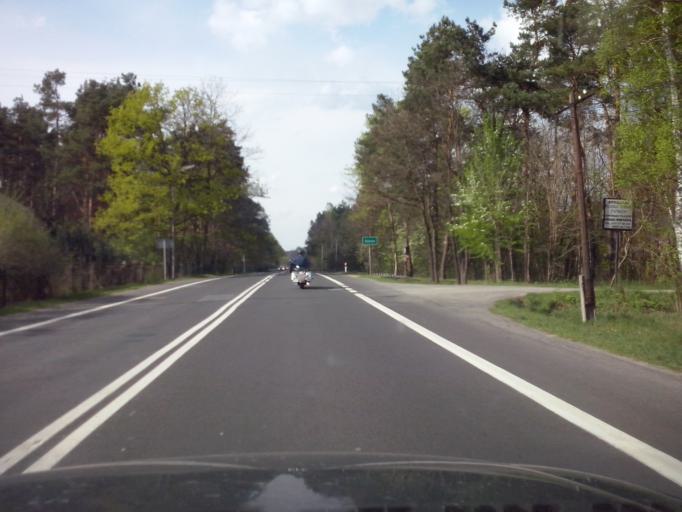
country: PL
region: Subcarpathian Voivodeship
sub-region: Powiat rzeszowski
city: Gorno
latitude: 50.2816
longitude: 22.1369
